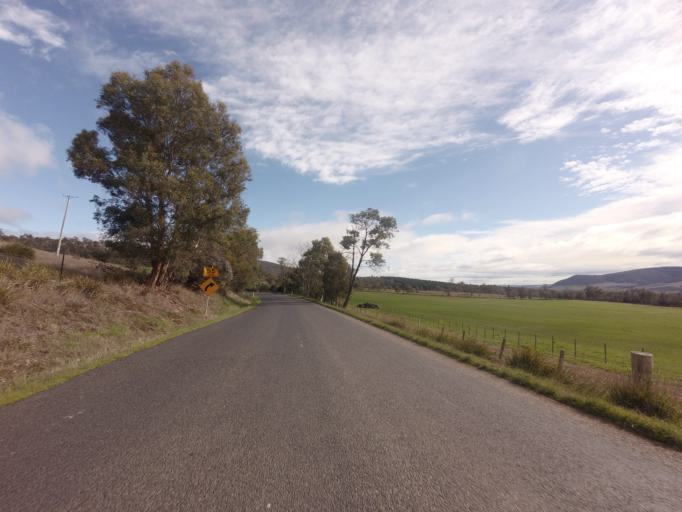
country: AU
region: Tasmania
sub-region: Derwent Valley
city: New Norfolk
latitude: -42.7781
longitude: 146.9842
